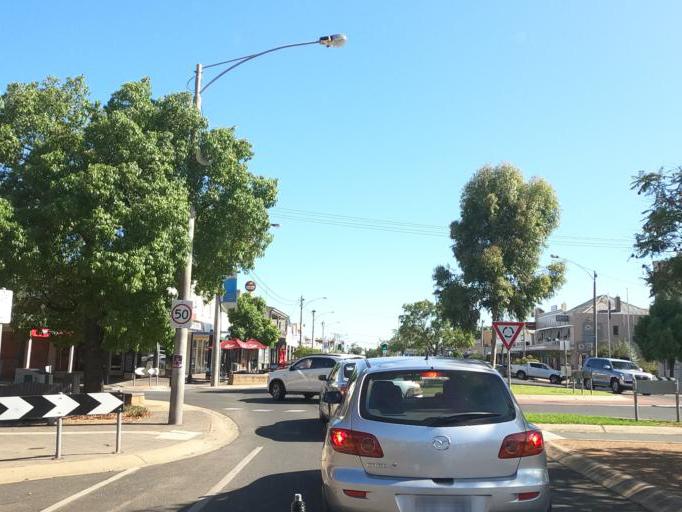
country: AU
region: Victoria
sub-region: Moira
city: Yarrawonga
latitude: -36.0133
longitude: 146.0044
